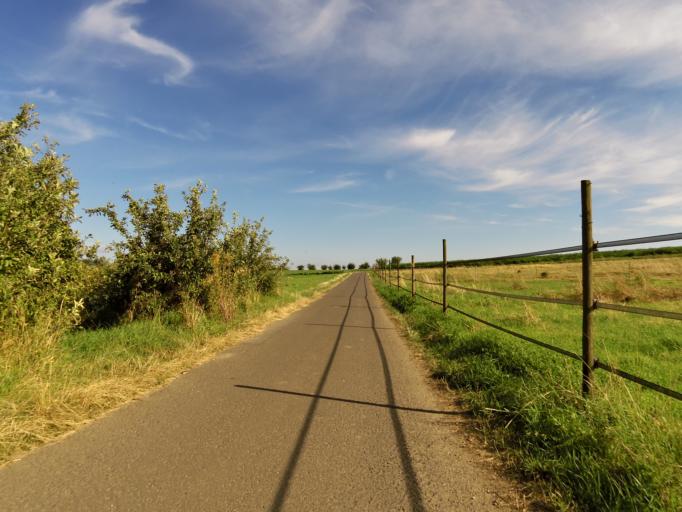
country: DE
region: Rheinland-Pfalz
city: Kirchheim an der Weinstrasse
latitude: 49.5403
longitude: 8.1911
